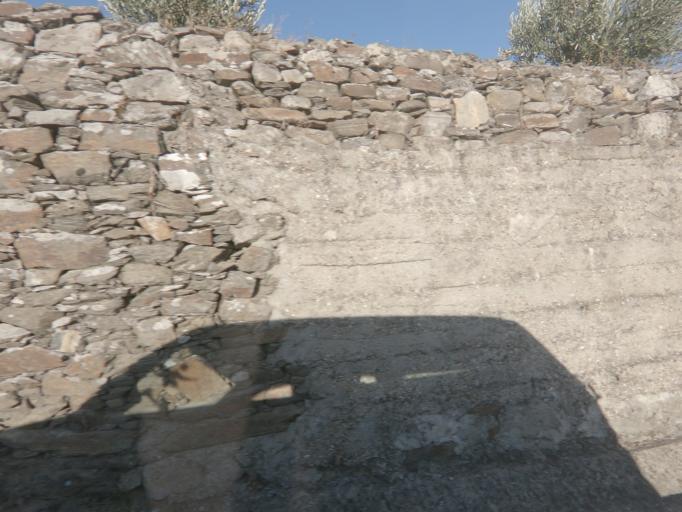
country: PT
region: Vila Real
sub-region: Peso da Regua
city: Godim
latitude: 41.1593
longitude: -7.8158
